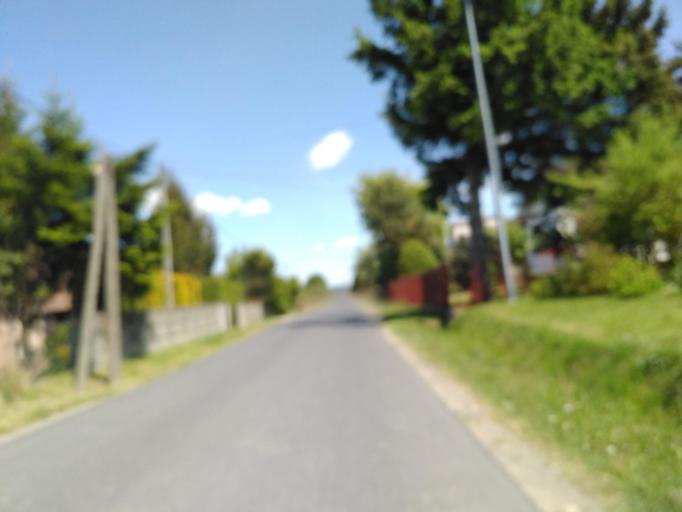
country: PL
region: Subcarpathian Voivodeship
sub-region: Powiat krosnienski
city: Jedlicze
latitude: 49.7025
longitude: 21.6860
